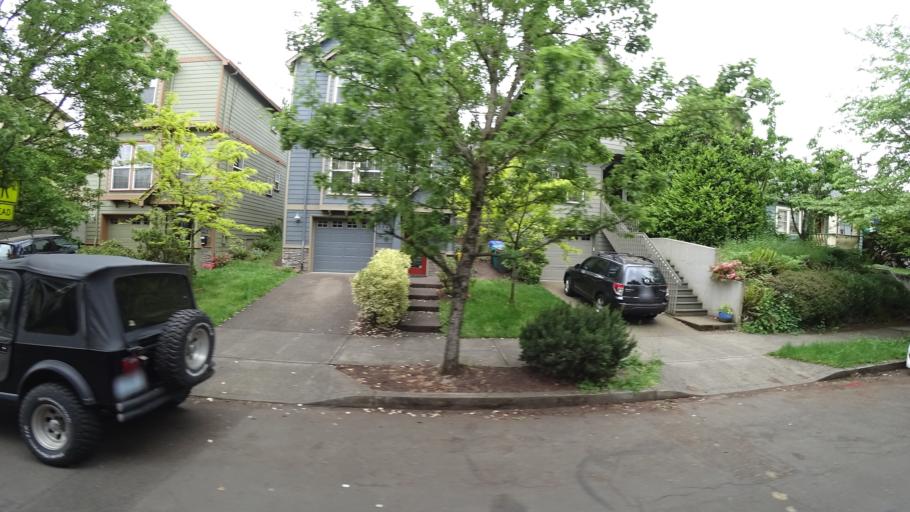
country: US
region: Oregon
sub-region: Multnomah County
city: Lents
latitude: 45.5214
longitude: -122.6062
